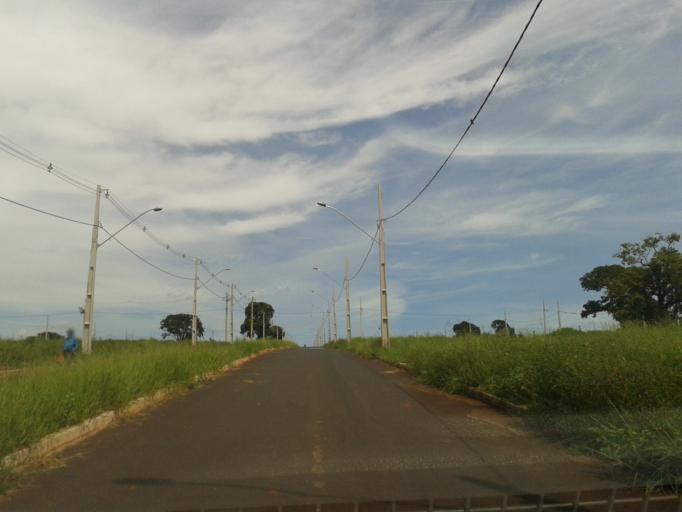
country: BR
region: Minas Gerais
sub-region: Santa Vitoria
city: Santa Vitoria
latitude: -18.8418
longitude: -50.1333
